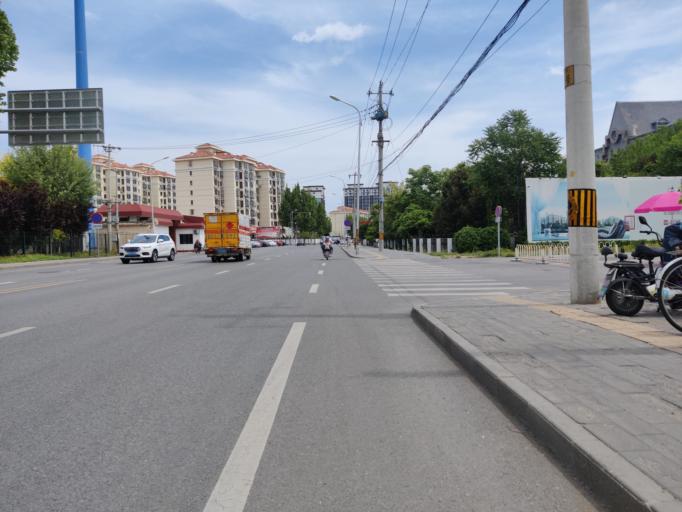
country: CN
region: Beijing
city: Miaocheng
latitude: 40.2878
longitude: 116.6374
